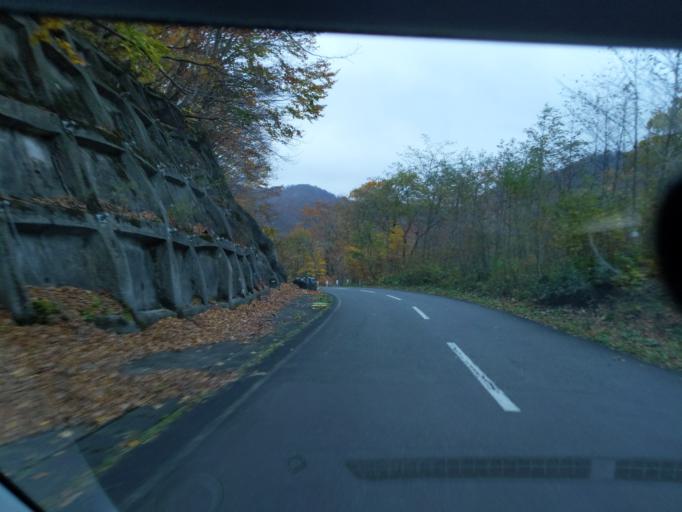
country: JP
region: Iwate
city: Mizusawa
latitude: 39.1167
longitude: 140.8435
